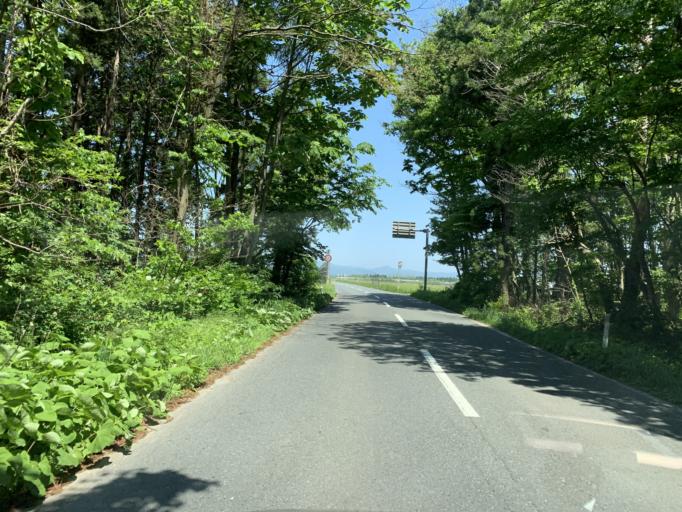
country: JP
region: Iwate
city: Kitakami
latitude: 39.2668
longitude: 141.0582
